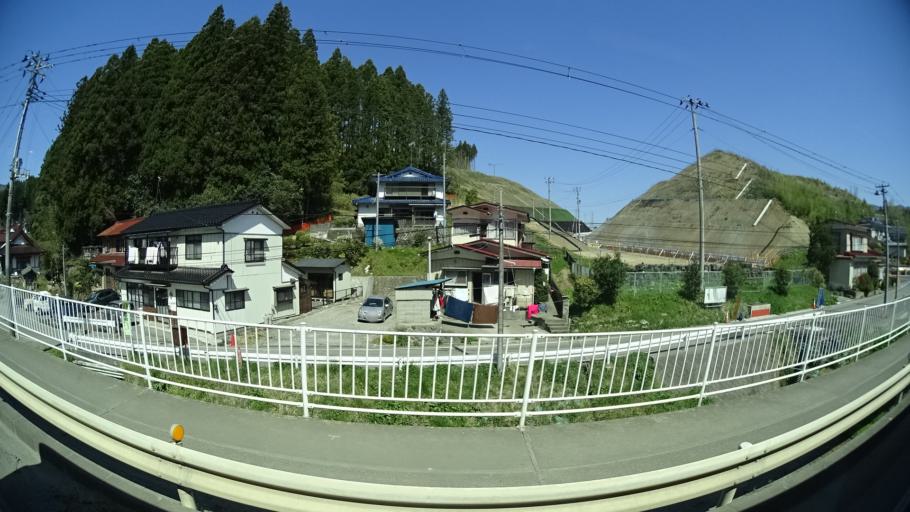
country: JP
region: Iwate
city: Ofunato
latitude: 38.9961
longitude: 141.6210
